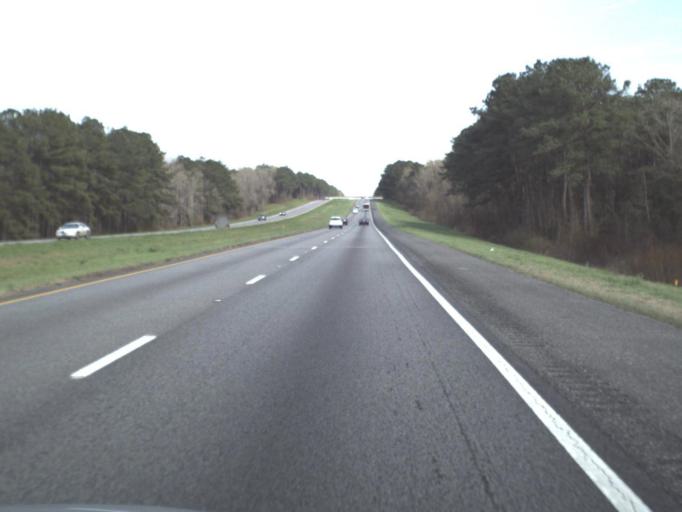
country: US
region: Florida
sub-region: Leon County
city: Tallahassee
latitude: 30.4780
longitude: -84.1039
